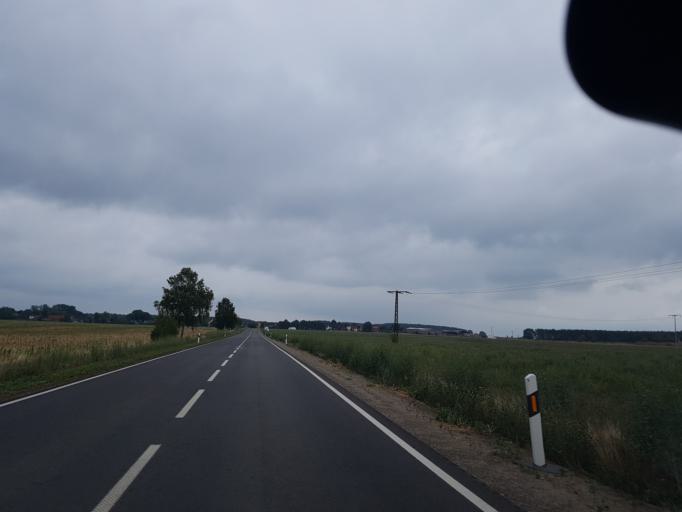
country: DE
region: Saxony-Anhalt
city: Tucheim
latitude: 52.2124
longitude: 12.1550
